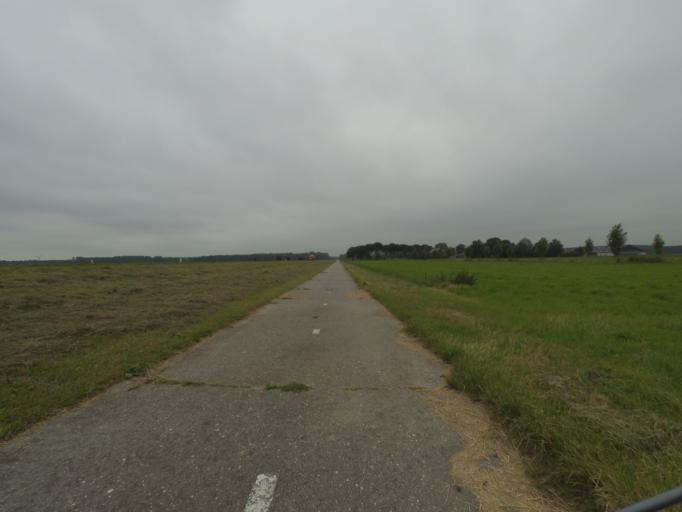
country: NL
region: Flevoland
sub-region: Gemeente Lelystad
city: Lelystad
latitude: 52.4288
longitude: 5.5234
